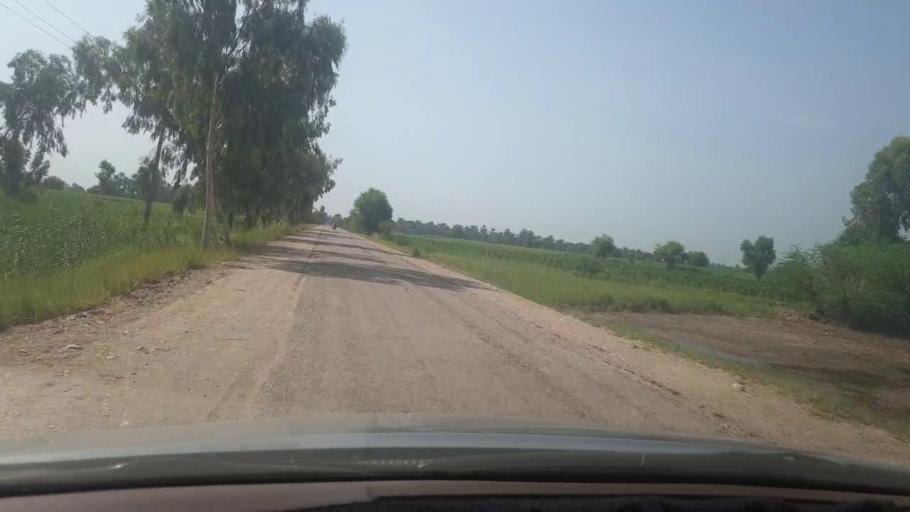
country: PK
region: Sindh
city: Ranipur
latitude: 27.2907
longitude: 68.5758
